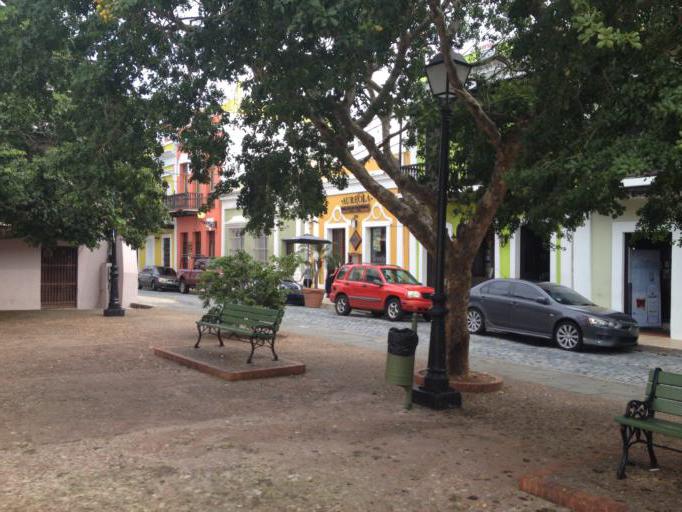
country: PR
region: San Juan
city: San Juan
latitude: 18.4672
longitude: -66.1183
